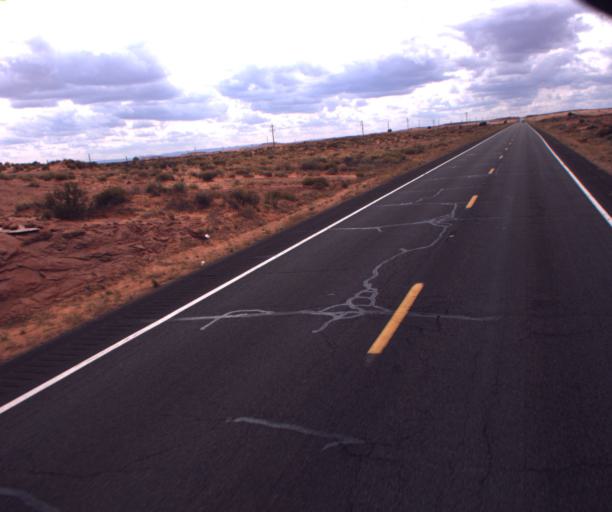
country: US
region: Arizona
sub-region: Navajo County
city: Kayenta
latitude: 36.9362
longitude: -109.7402
